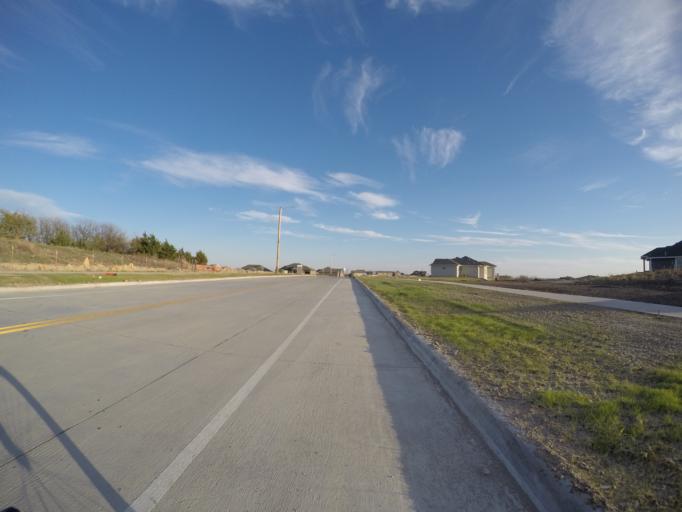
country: US
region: Kansas
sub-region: Riley County
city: Manhattan
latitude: 39.1747
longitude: -96.6364
